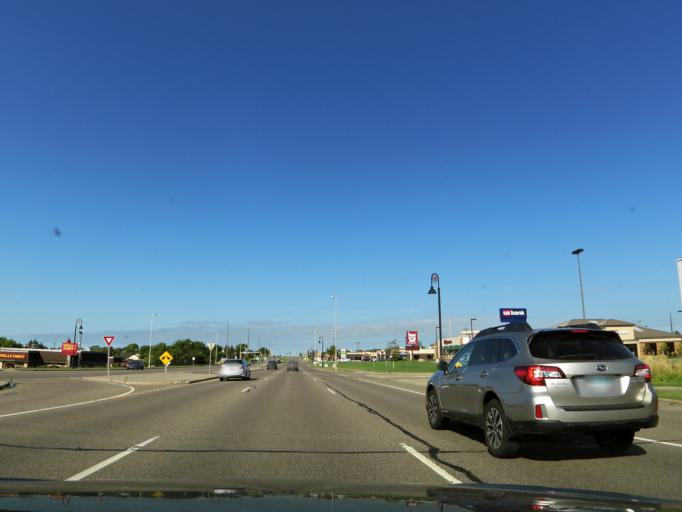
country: US
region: Minnesota
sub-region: Dakota County
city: Burnsville
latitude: 44.7465
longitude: -93.2896
